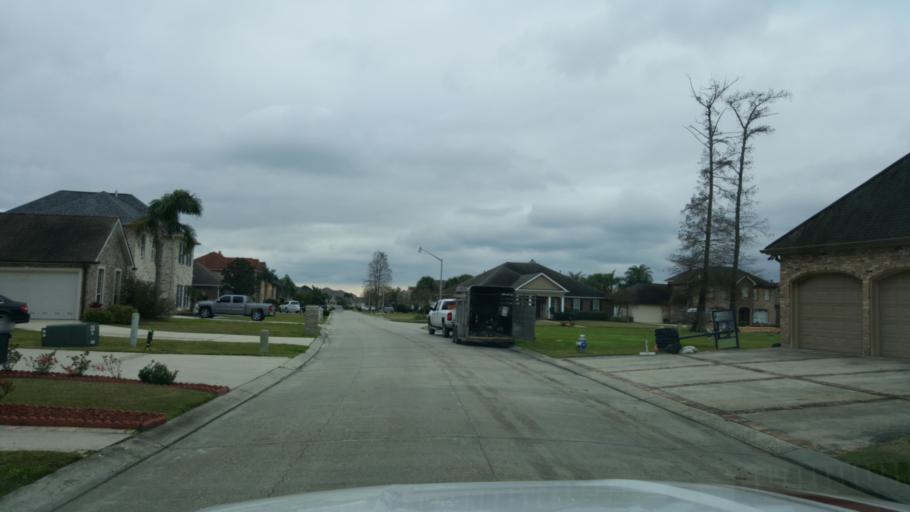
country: US
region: Louisiana
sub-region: Jefferson Parish
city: Harvey
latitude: 29.8810
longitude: -90.0785
